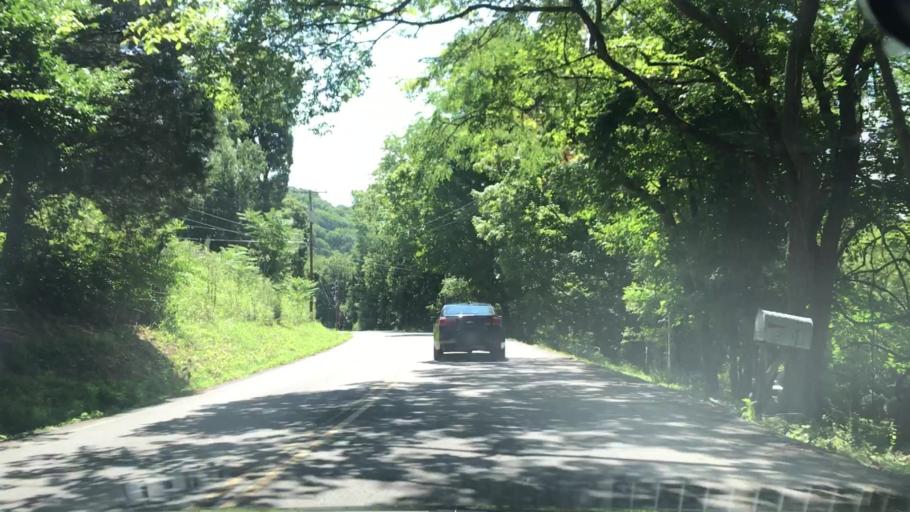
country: US
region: Tennessee
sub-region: Williamson County
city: Franklin
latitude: 35.9646
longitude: -86.8582
